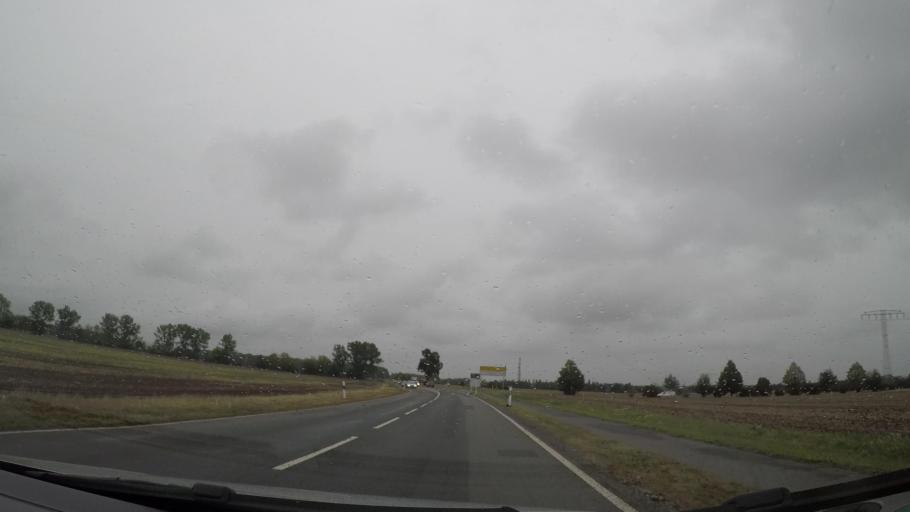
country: DE
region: Saxony-Anhalt
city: Ebendorf
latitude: 52.1737
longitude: 11.5906
